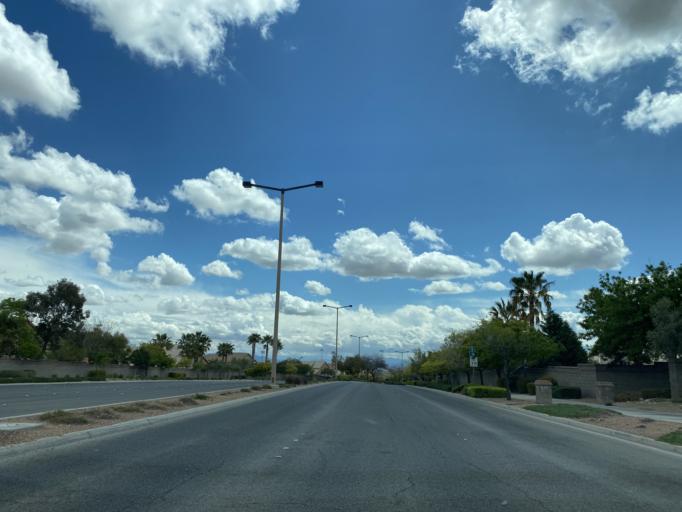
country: US
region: Nevada
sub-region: Clark County
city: Summerlin South
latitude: 36.1849
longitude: -115.3263
